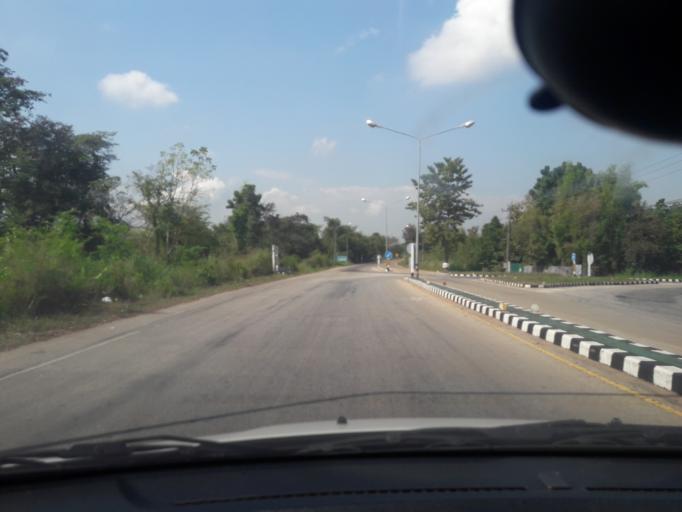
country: TH
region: Lampang
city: Mae Tha
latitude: 18.1981
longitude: 99.5084
